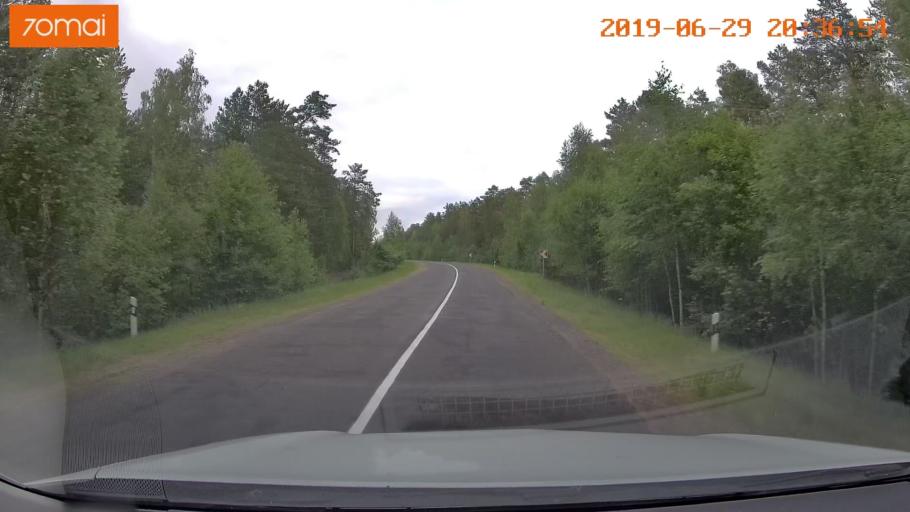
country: BY
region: Brest
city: Hantsavichy
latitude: 52.5315
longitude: 26.3622
